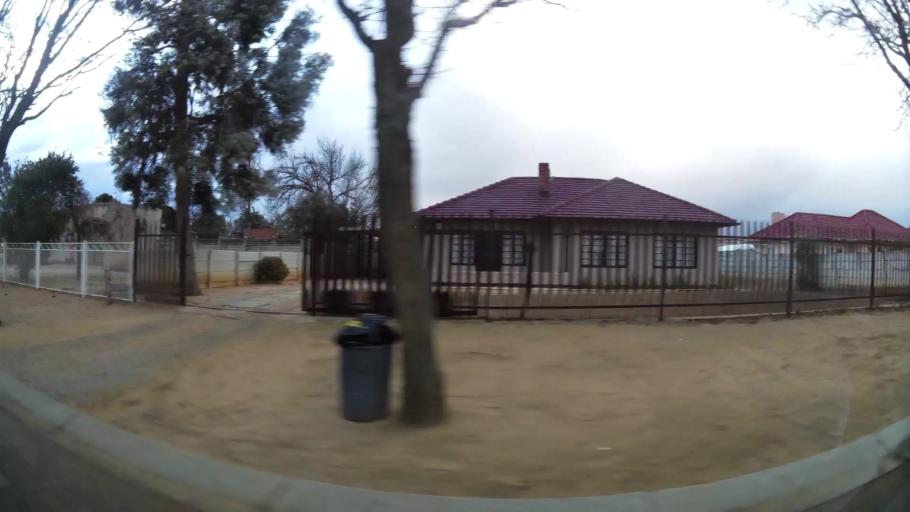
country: ZA
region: Orange Free State
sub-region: Lejweleputswa District Municipality
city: Welkom
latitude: -27.9694
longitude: 26.7658
